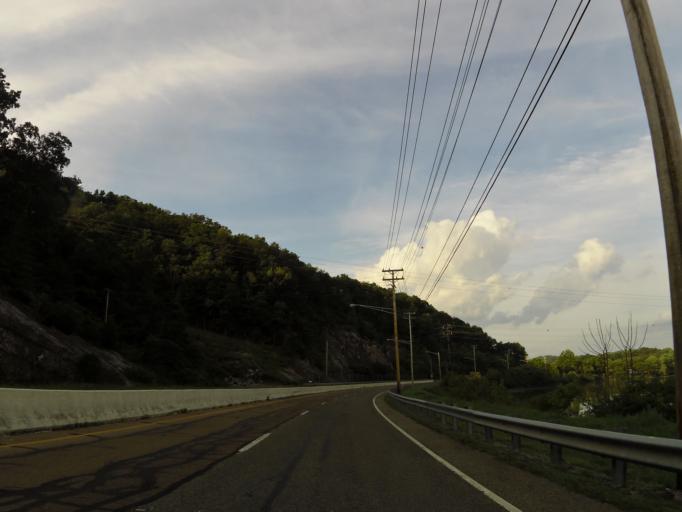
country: US
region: Tennessee
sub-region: Anderson County
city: Clinton
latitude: 36.0869
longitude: -84.1591
